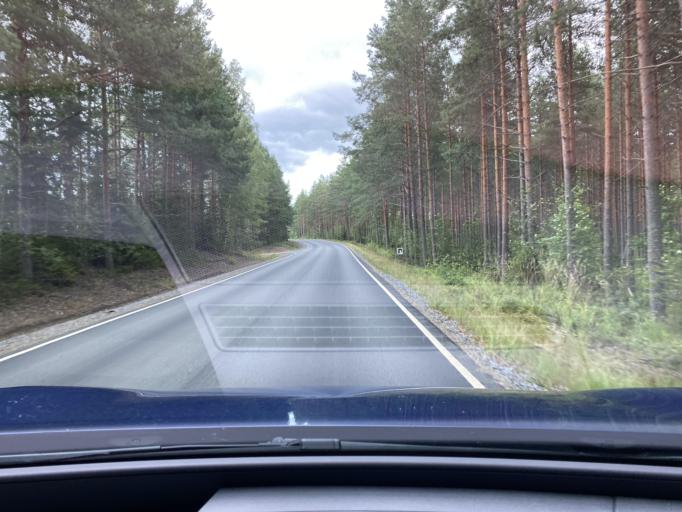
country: FI
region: Pirkanmaa
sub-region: Lounais-Pirkanmaa
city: Vammala
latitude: 61.2871
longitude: 23.0166
